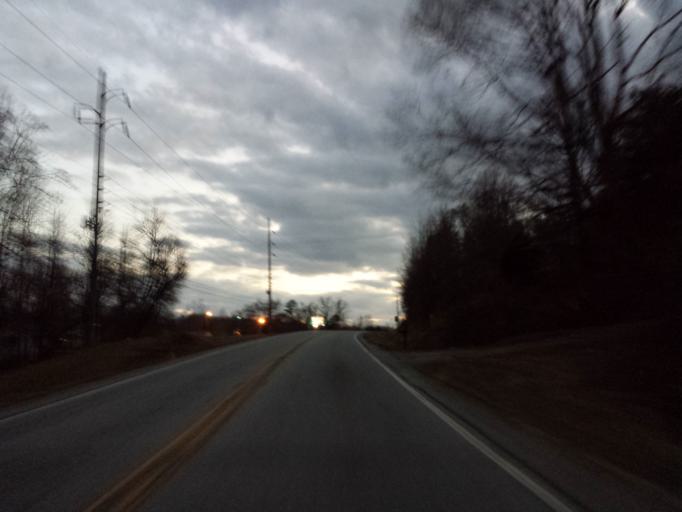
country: US
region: Georgia
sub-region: White County
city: Cleveland
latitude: 34.6467
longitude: -83.7363
